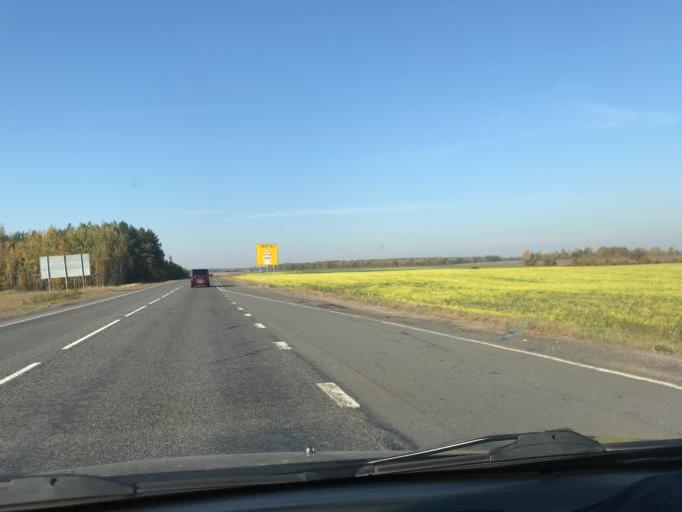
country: BY
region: Mogilev
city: Babruysk
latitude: 53.0843
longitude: 29.0650
